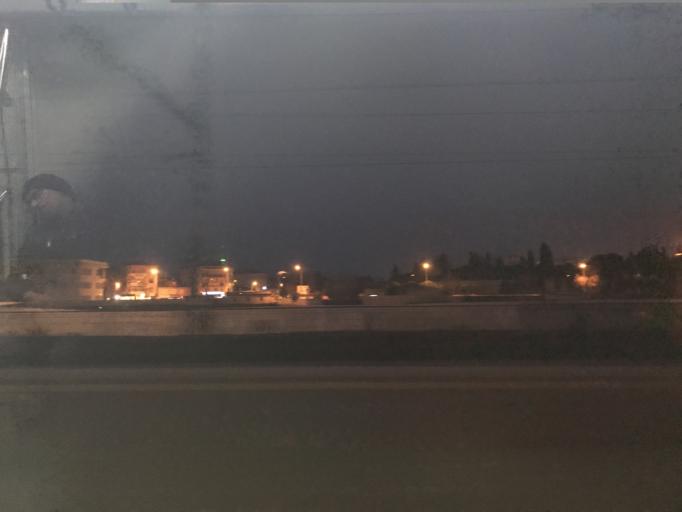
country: TR
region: Istanbul
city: Icmeler
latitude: 40.8463
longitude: 29.2995
